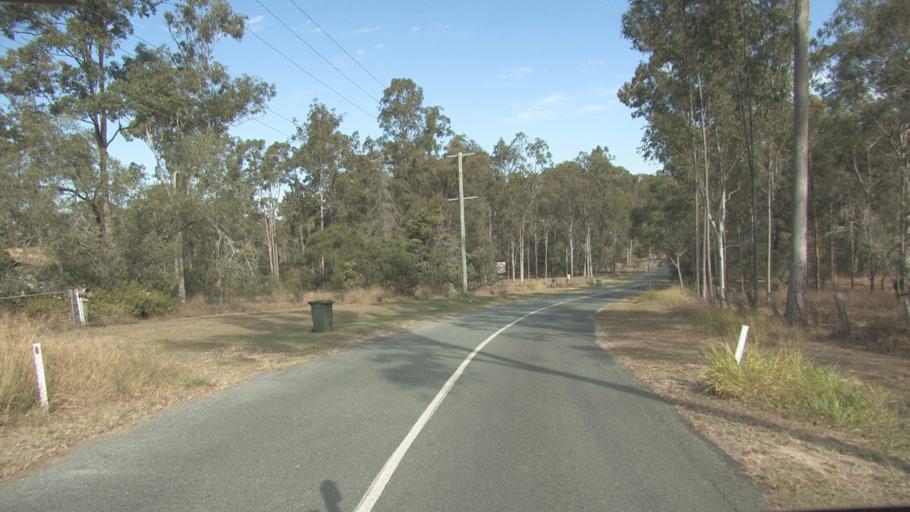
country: AU
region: Queensland
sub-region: Logan
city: North Maclean
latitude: -27.7389
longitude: 152.9787
